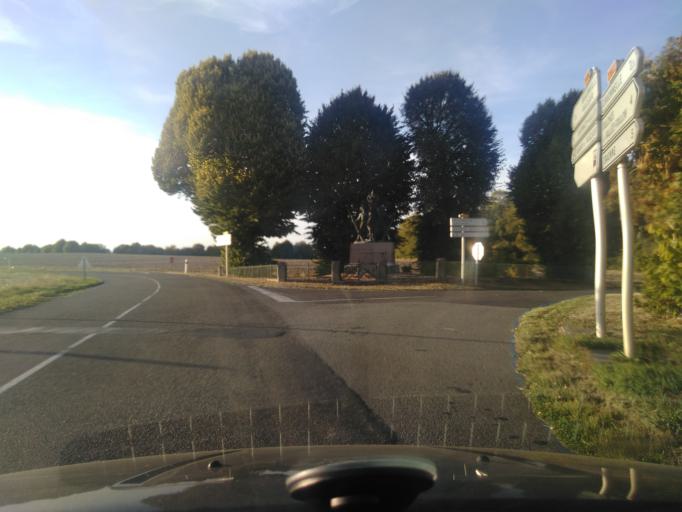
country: FR
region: Picardie
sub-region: Departement de l'Aisne
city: Bruyeres-et-Montberault
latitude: 49.4407
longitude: 3.7381
